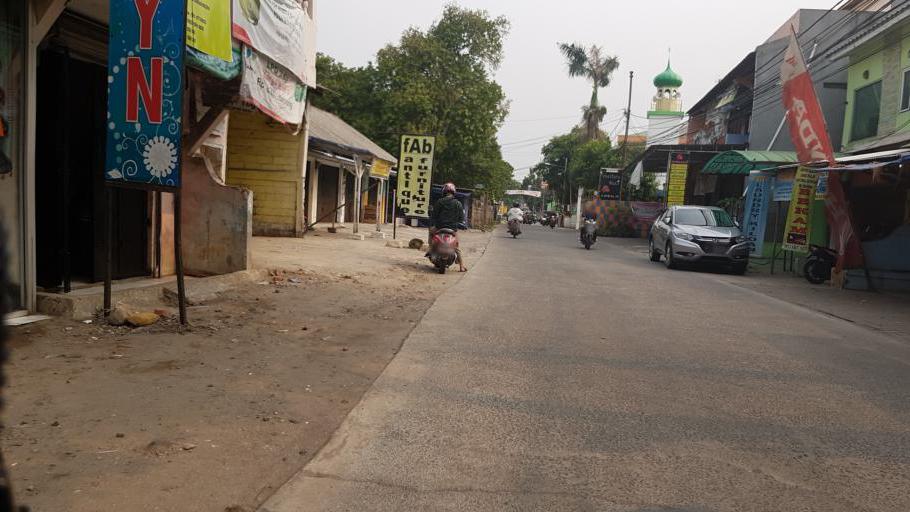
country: ID
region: West Java
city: Depok
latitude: -6.3679
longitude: 106.8427
